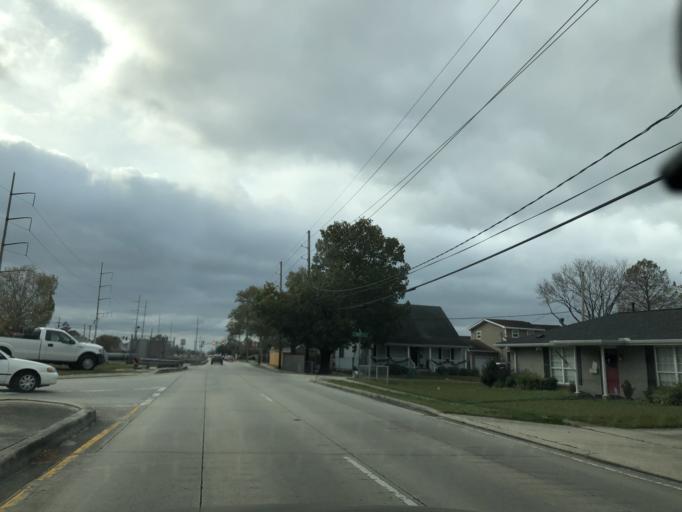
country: US
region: Louisiana
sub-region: Jefferson Parish
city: Metairie Terrace
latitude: 29.9931
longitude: -90.1691
